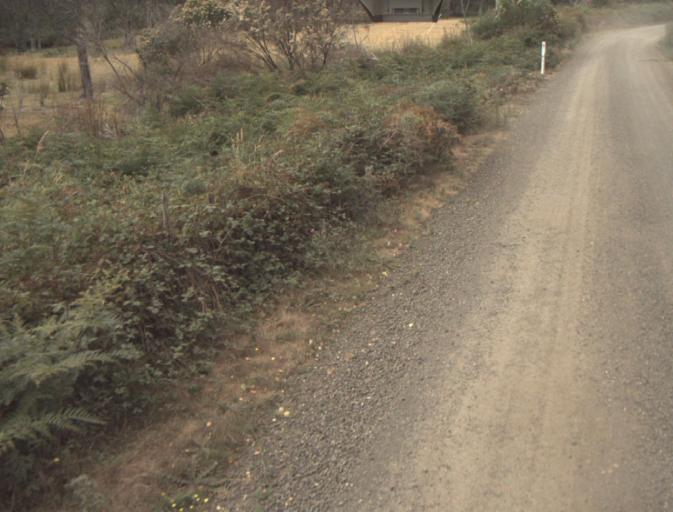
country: AU
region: Tasmania
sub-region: Dorset
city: Bridport
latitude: -41.1930
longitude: 147.2629
